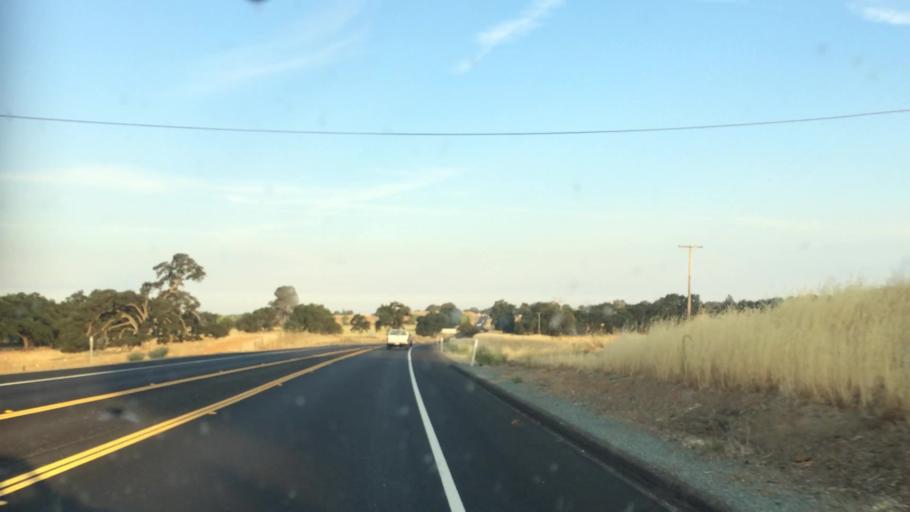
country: US
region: California
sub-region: Amador County
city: Plymouth
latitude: 38.4499
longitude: -120.8992
